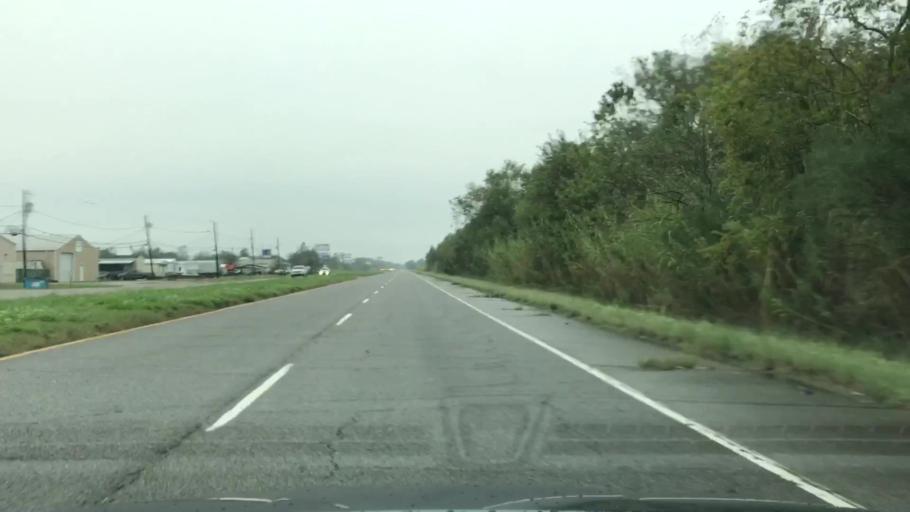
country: US
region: Louisiana
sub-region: Saint Charles Parish
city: Des Allemands
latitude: 29.8087
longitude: -90.4951
